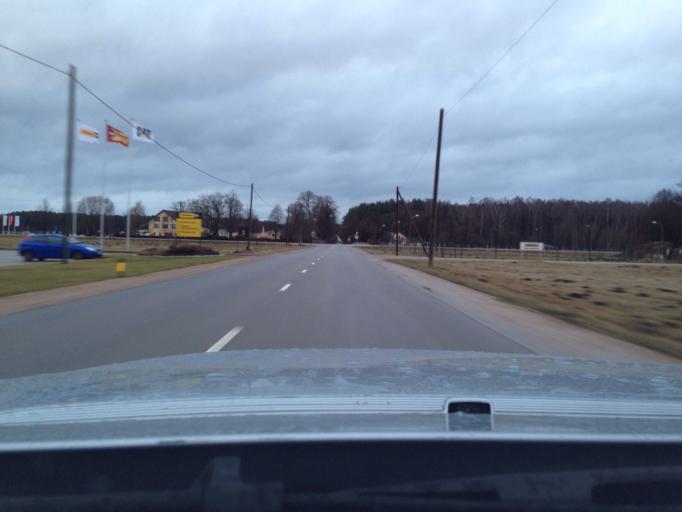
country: LV
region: Marupe
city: Marupe
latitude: 56.8822
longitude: 23.9782
